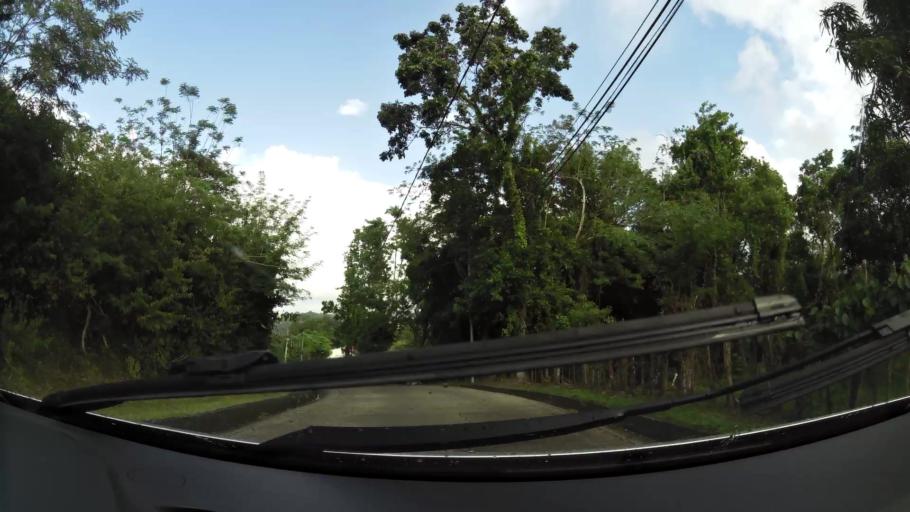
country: MQ
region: Martinique
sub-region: Martinique
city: Saint-Esprit
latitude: 14.5075
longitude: -60.9620
